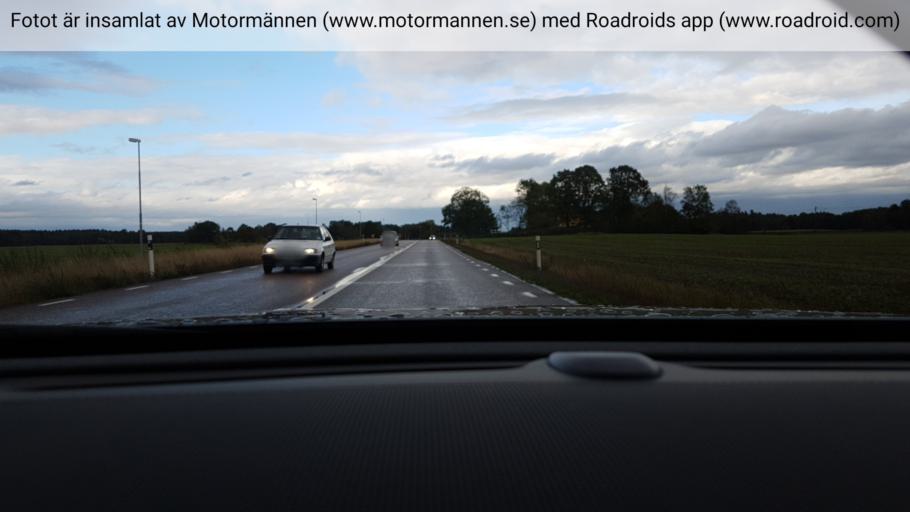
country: SE
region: Vaestra Goetaland
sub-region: Vanersborgs Kommun
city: Bralanda
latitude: 58.5027
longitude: 12.2822
